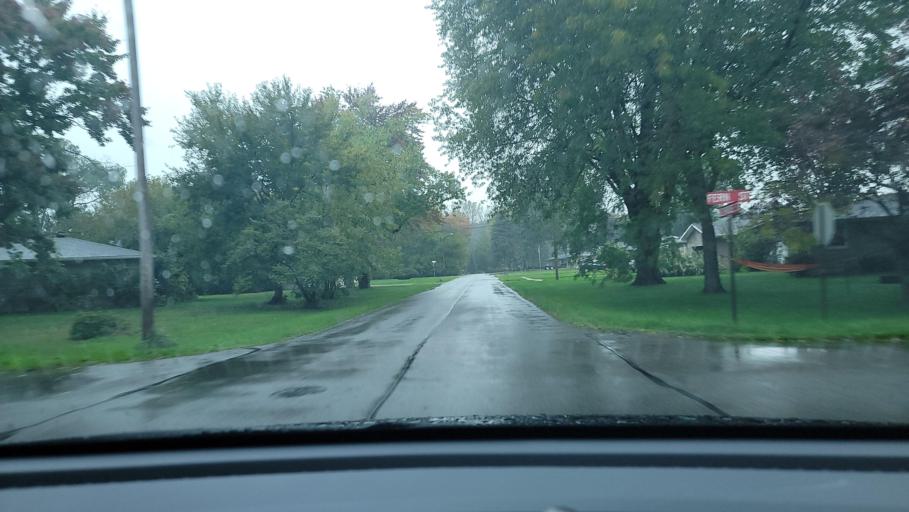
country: US
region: Indiana
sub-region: Porter County
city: Portage
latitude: 41.5659
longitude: -87.1944
